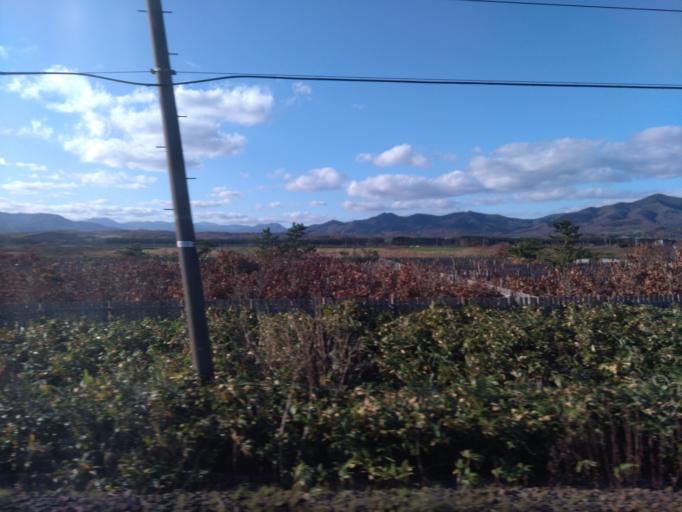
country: JP
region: Hokkaido
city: Niseko Town
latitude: 42.5421
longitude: 140.4080
